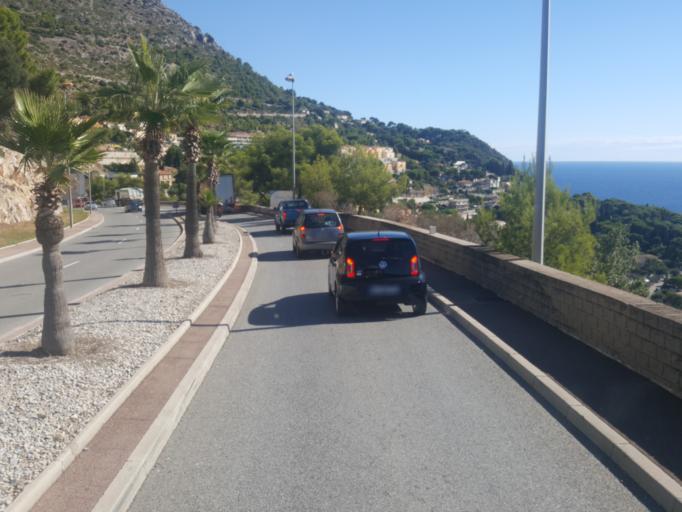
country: FR
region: Provence-Alpes-Cote d'Azur
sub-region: Departement des Alpes-Maritimes
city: Cap-d'Ail
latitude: 43.7247
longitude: 7.3928
